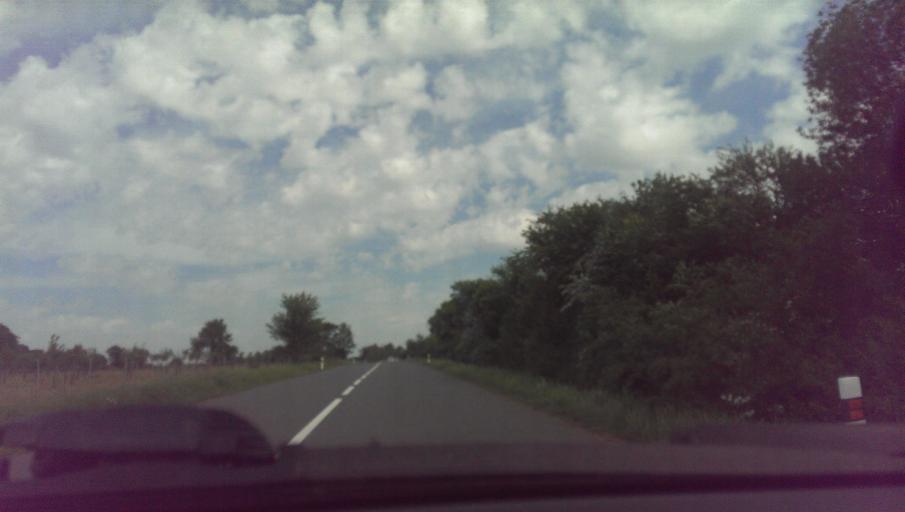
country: CZ
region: Zlin
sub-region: Okres Zlin
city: Otrokovice
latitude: 49.2385
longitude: 17.5381
